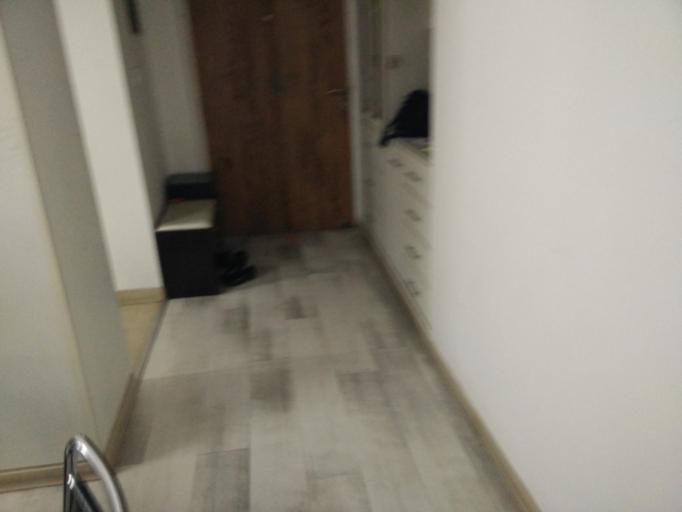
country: IN
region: Haryana
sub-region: Gurgaon
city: Gurgaon
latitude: 28.4569
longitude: 77.0674
